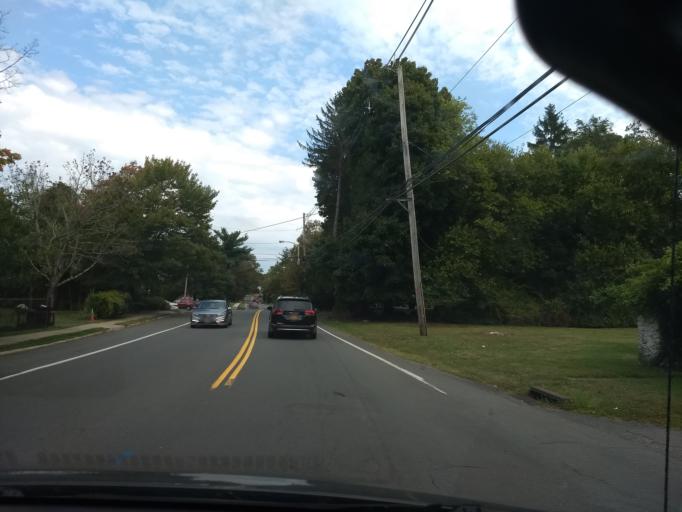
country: US
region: New York
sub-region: Rockland County
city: Spring Valley
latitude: 41.1004
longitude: -74.0509
